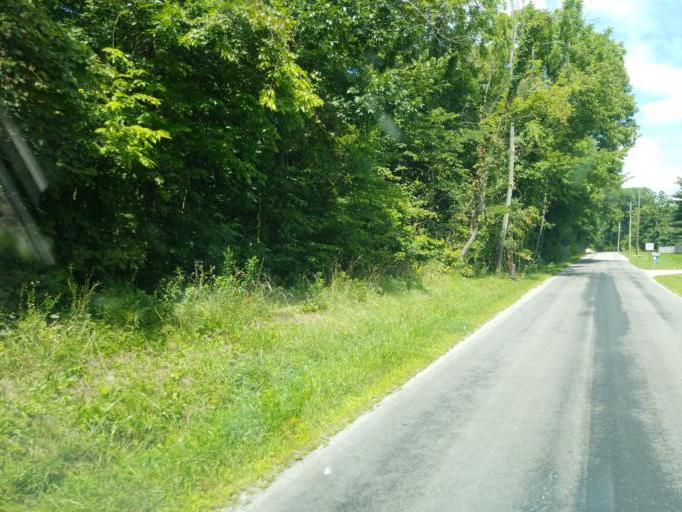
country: US
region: Ohio
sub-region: Delaware County
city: Sunbury
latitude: 40.2799
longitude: -82.8313
